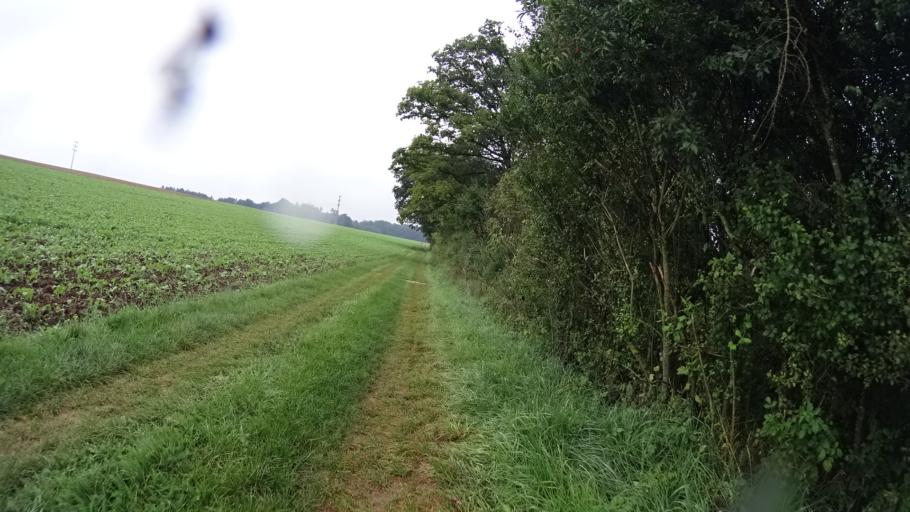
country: DE
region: Bavaria
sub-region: Upper Bavaria
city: Bohmfeld
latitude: 48.9107
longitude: 11.3843
